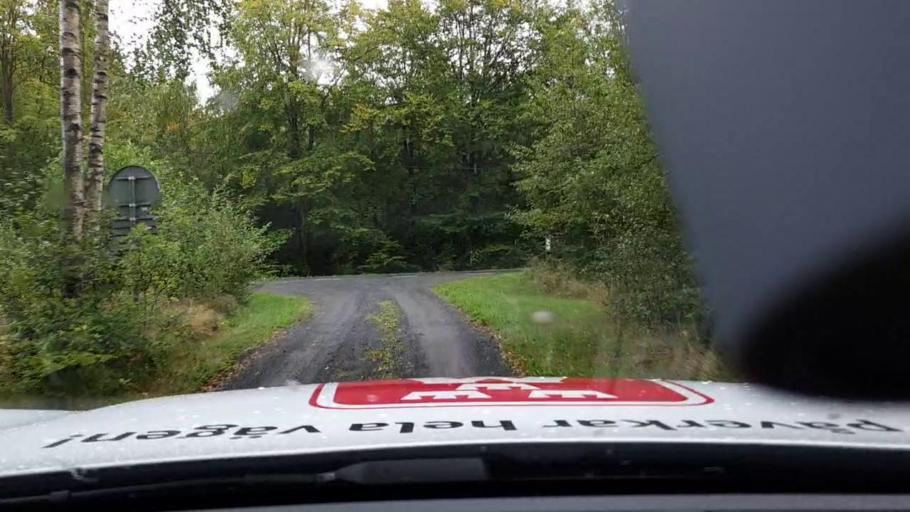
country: SE
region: Skane
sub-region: Hassleholms Kommun
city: Vinslov
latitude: 56.0403
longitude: 13.8695
